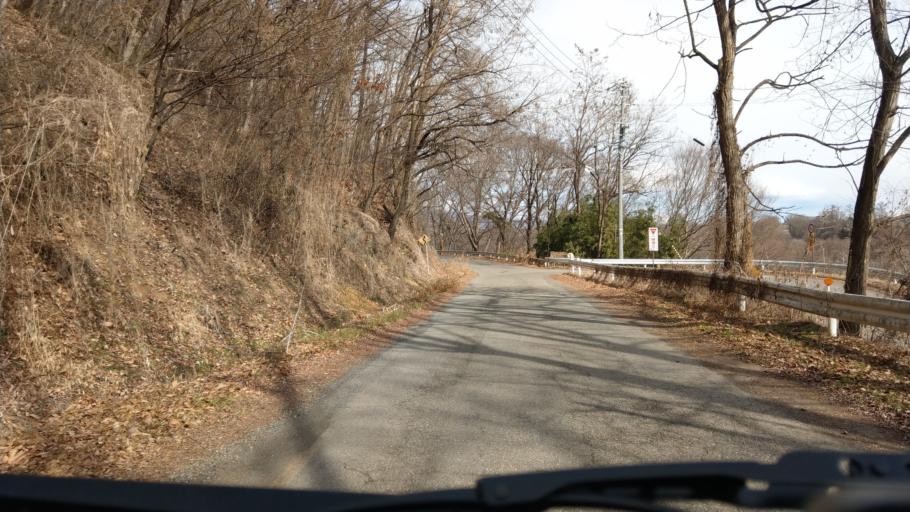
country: JP
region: Nagano
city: Komoro
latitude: 36.2870
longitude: 138.4142
